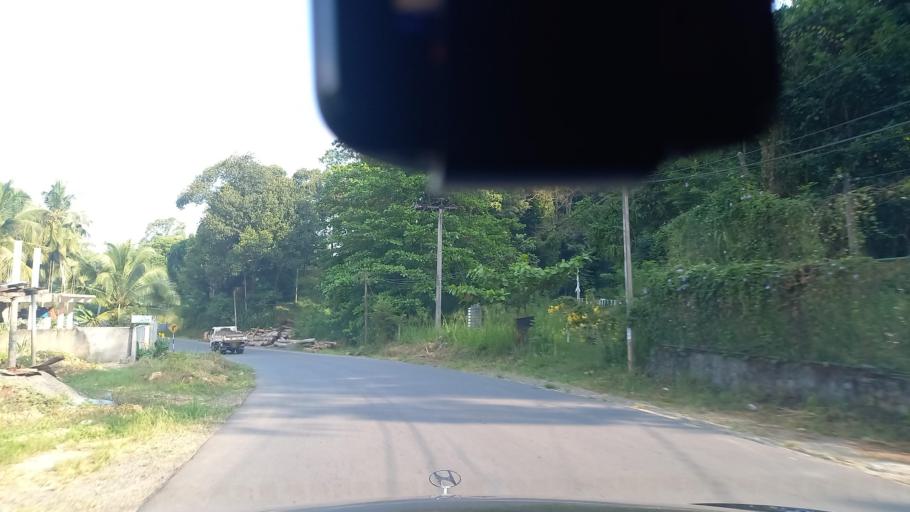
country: LK
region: Central
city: Gampola
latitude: 7.2293
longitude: 80.6038
